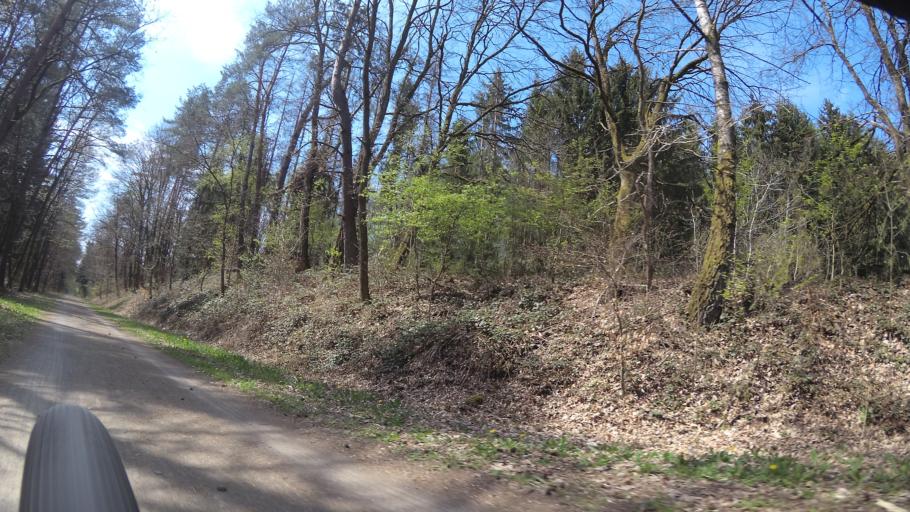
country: DE
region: Rheinland-Pfalz
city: Schonenberg-Kubelberg
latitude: 49.3957
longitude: 7.3587
